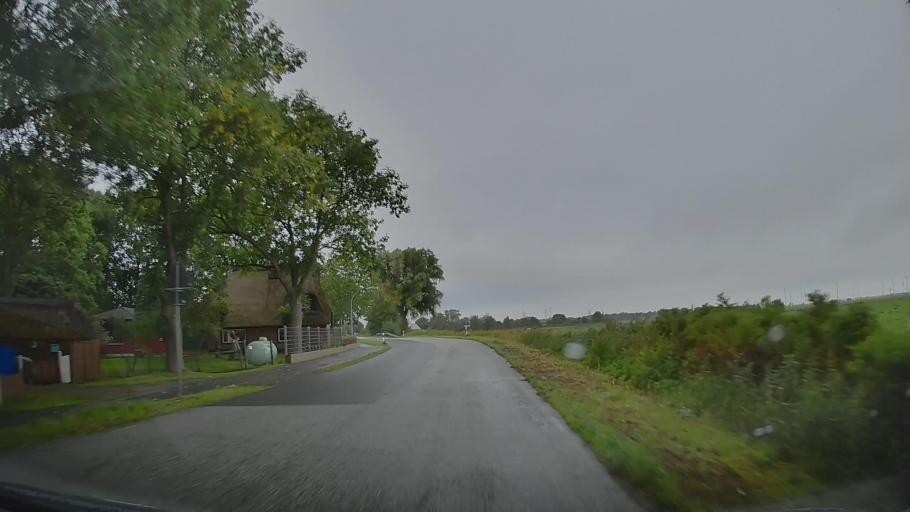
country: DE
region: Schleswig-Holstein
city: Sankt Margarethen
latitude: 53.8799
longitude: 9.2630
